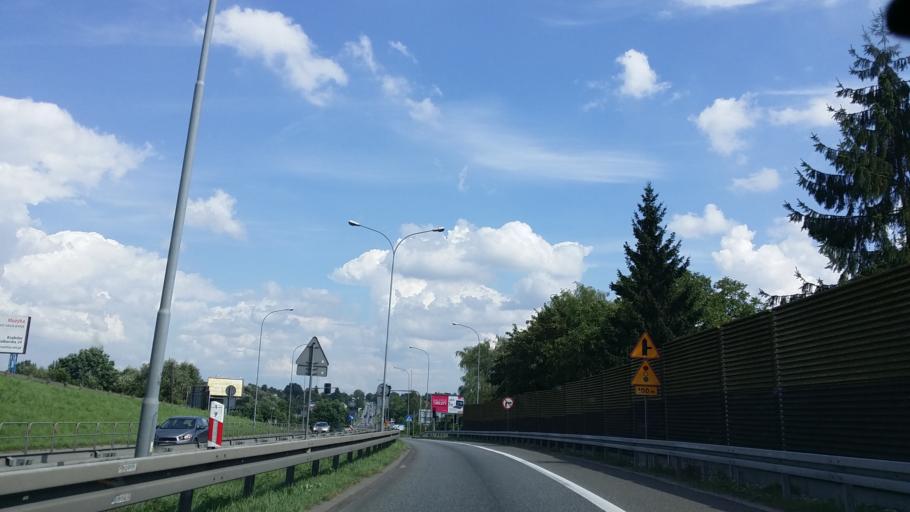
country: PL
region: Lesser Poland Voivodeship
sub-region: Powiat wielicki
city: Wieliczka
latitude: 49.9943
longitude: 20.0402
